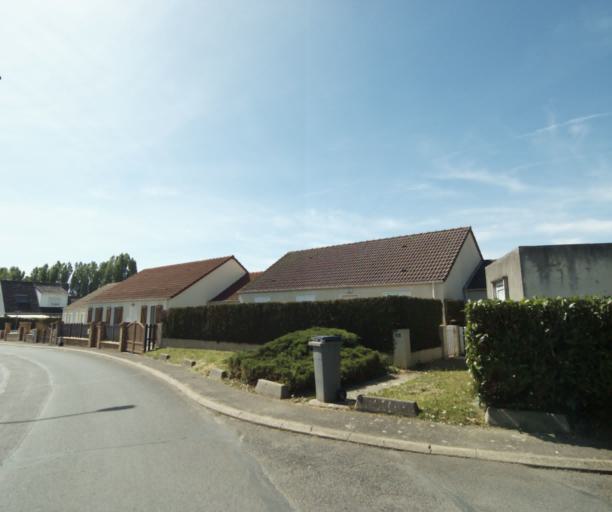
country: FR
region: Ile-de-France
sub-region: Departement de Seine-et-Marne
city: Nangis
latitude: 48.5551
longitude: 3.0090
